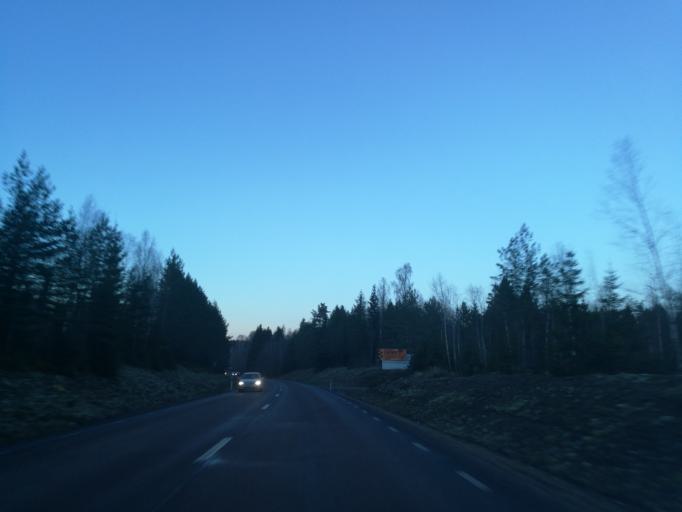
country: SE
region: Vaermland
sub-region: Eda Kommun
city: Charlottenberg
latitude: 59.9145
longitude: 12.2748
